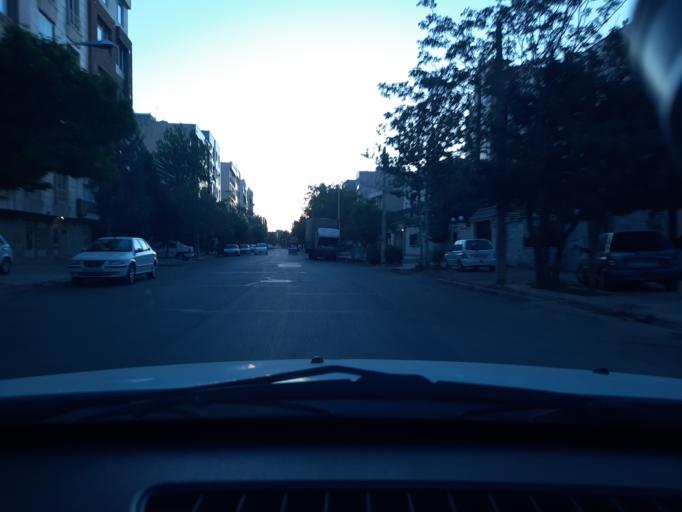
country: IR
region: Qazvin
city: Qazvin
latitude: 36.2991
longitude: 50.0149
